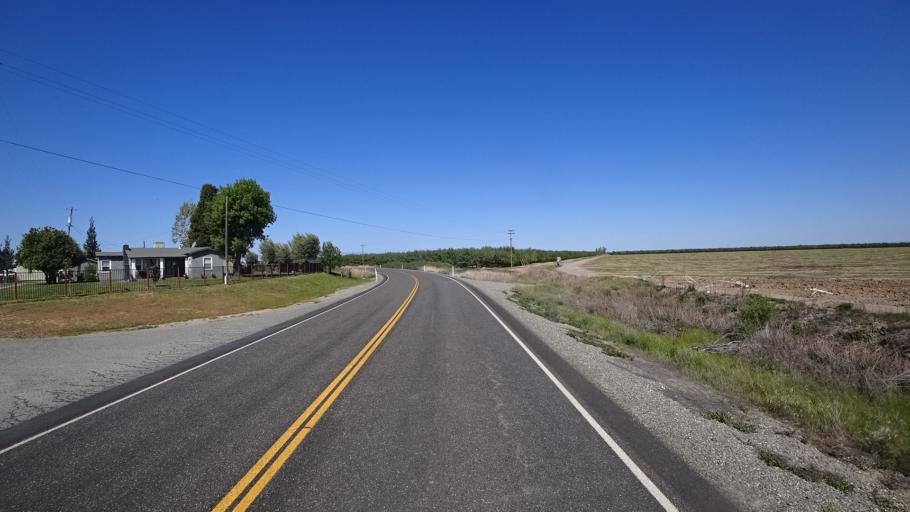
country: US
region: California
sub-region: Glenn County
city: Hamilton City
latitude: 39.7102
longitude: -122.0784
